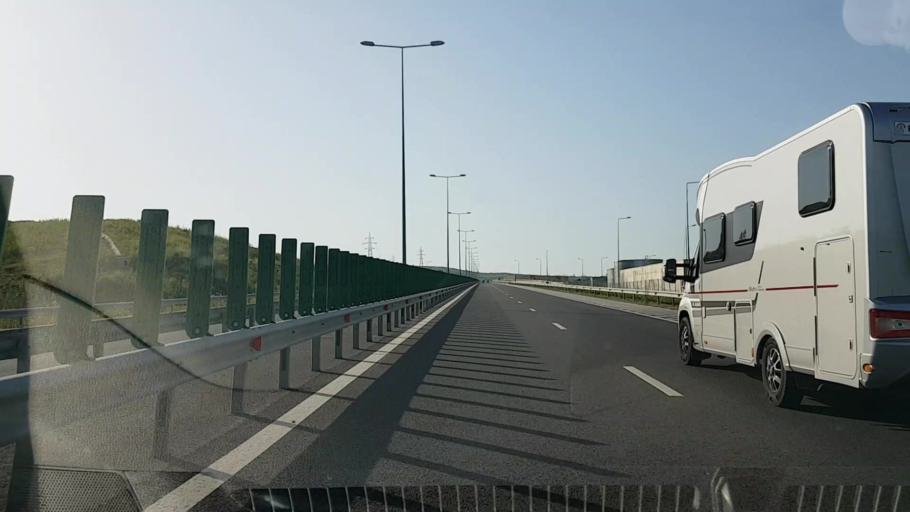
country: RO
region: Alba
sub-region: Comuna Unirea
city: Unirea
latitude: 46.4507
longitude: 23.7931
